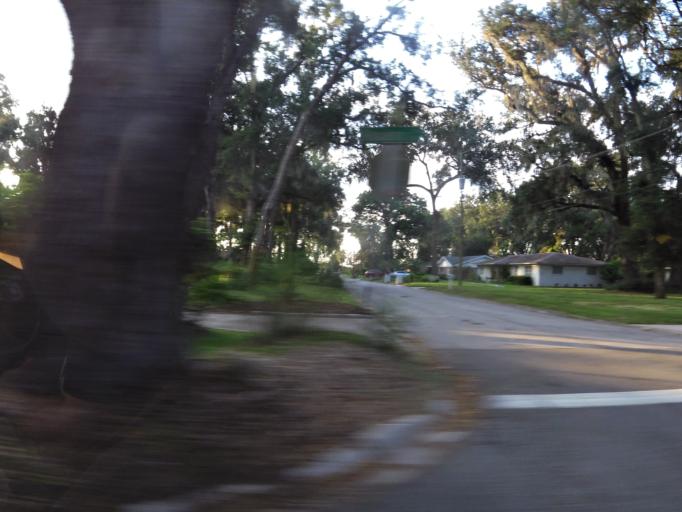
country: US
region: Florida
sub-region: Clay County
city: Orange Park
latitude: 30.2058
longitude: -81.6317
